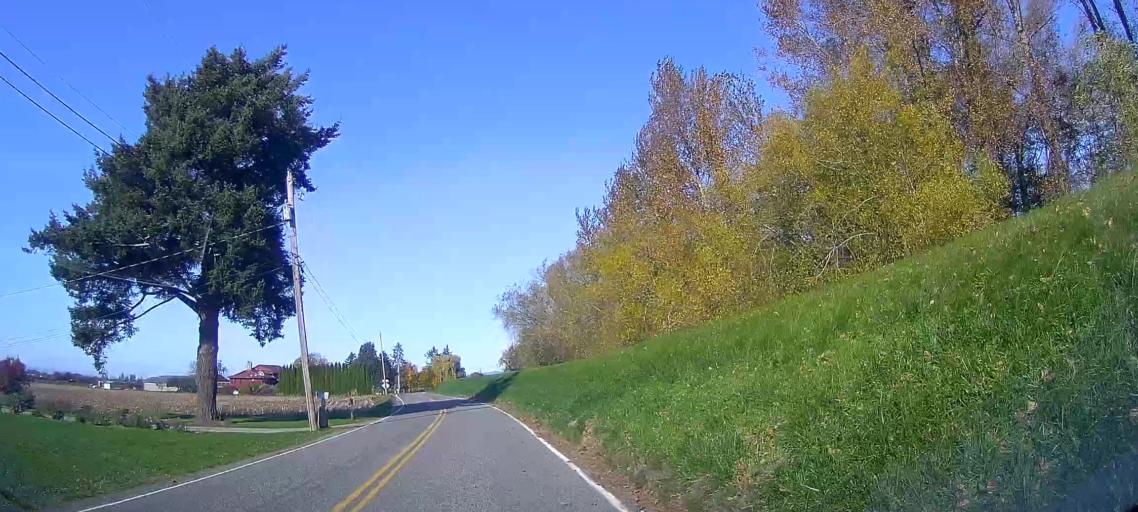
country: US
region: Washington
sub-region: Skagit County
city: Mount Vernon
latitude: 48.4074
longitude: -122.3679
